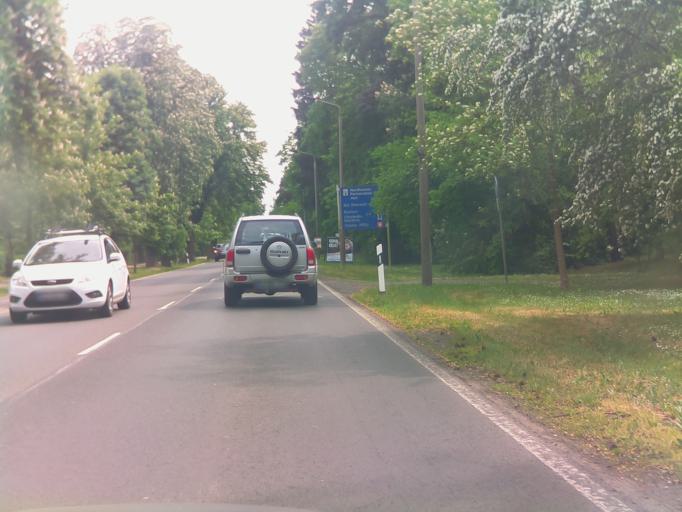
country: DE
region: Thuringia
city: Nordhausen
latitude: 51.5172
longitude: 10.7840
